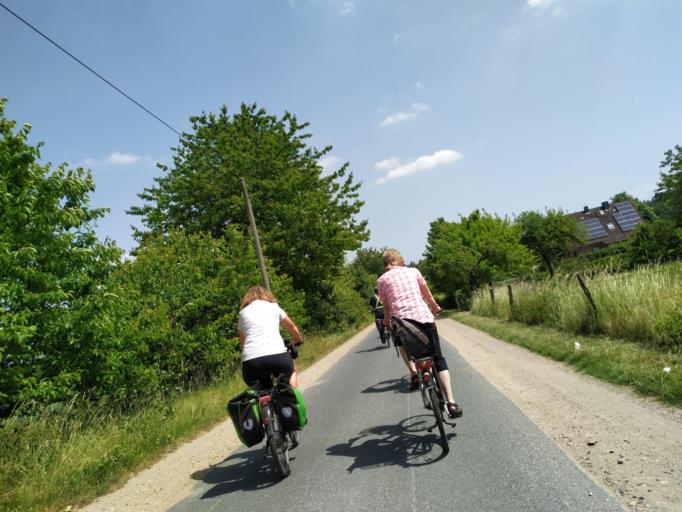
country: DE
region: Schleswig-Holstein
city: Fredeburg
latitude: 53.6710
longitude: 10.7358
